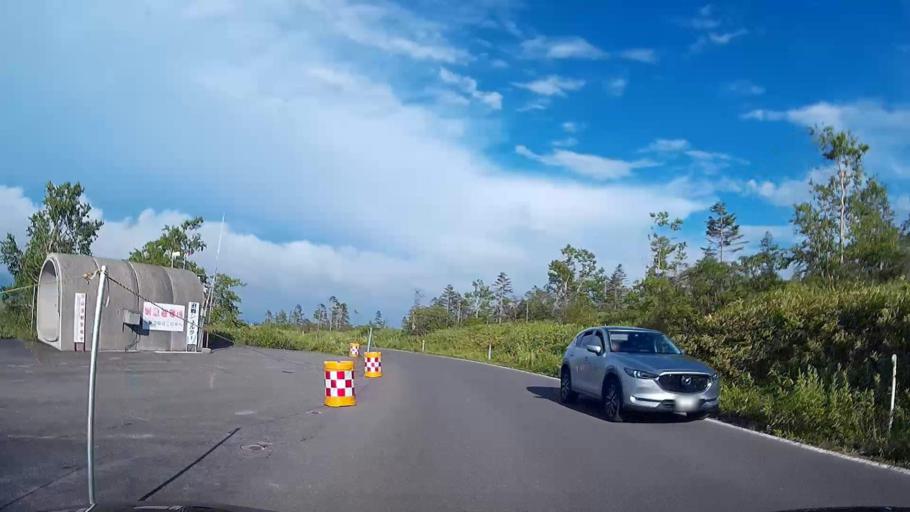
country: JP
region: Nagano
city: Nakano
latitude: 36.6369
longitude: 138.5364
